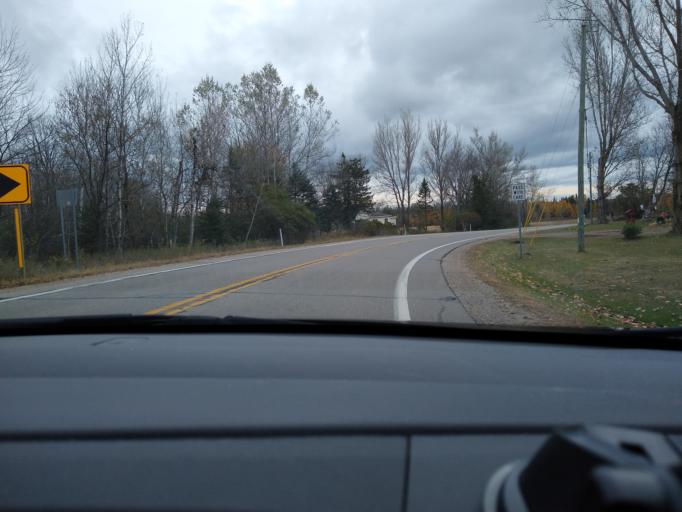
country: US
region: Michigan
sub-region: Delta County
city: Escanaba
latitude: 45.7375
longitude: -87.2641
